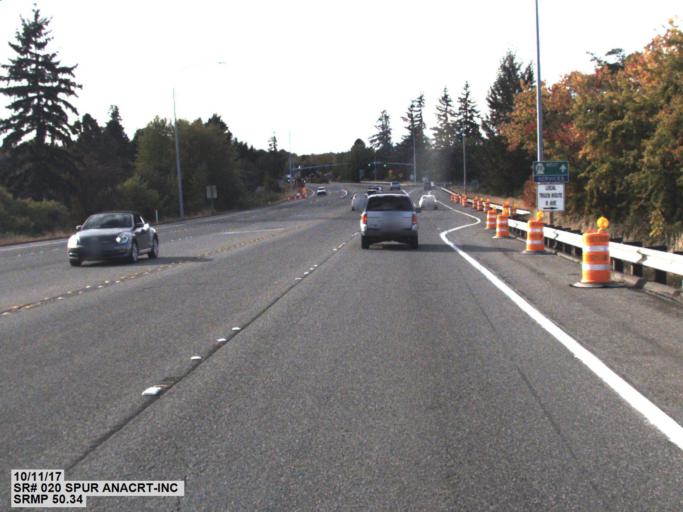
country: US
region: Washington
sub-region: Jefferson County
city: Port Hadlock-Irondale
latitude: 47.9990
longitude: -122.8429
